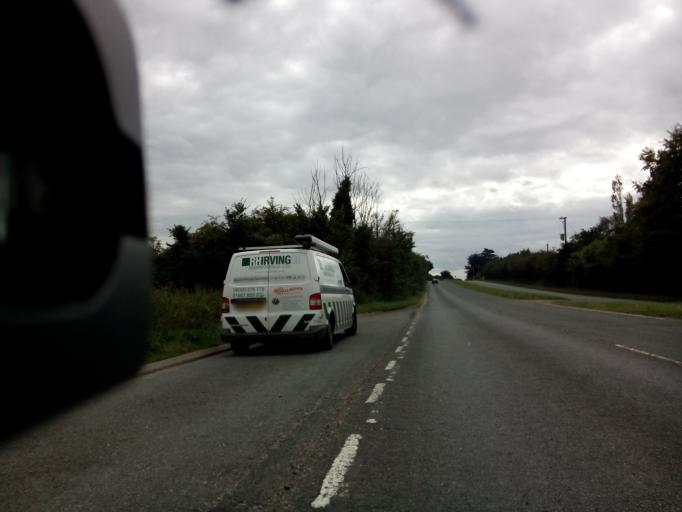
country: GB
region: England
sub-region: Suffolk
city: Capel Saint Mary
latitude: 52.0224
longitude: 1.0752
